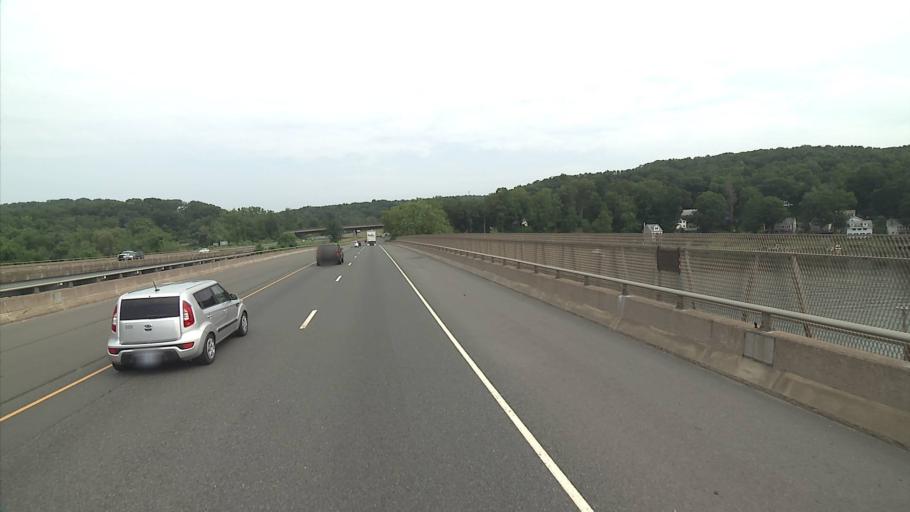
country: US
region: Connecticut
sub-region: New Haven County
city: Heritage Village
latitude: 41.4389
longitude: -73.2473
